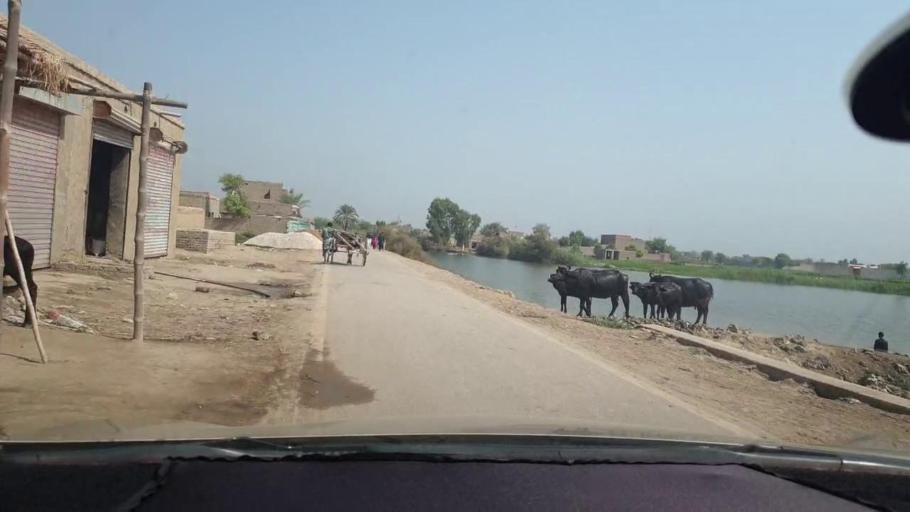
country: PK
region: Sindh
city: Kambar
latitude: 27.5787
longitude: 68.0067
